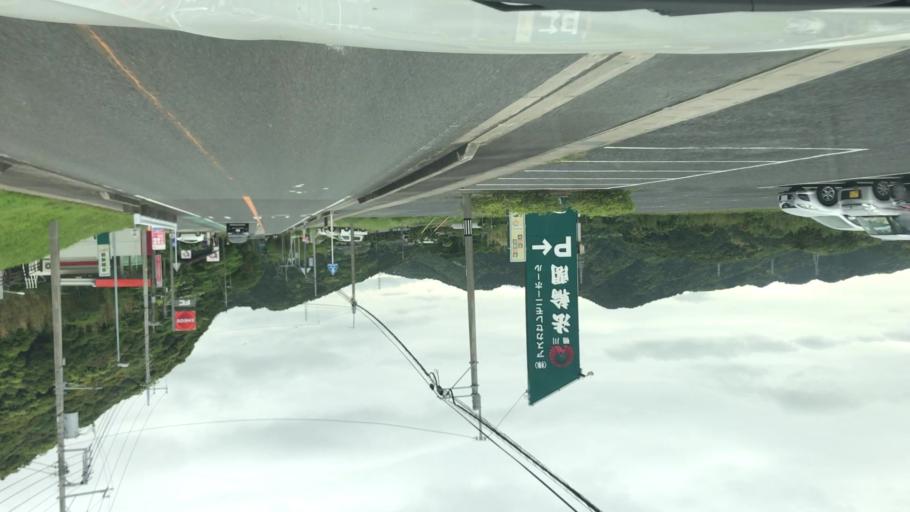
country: JP
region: Chiba
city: Kawaguchi
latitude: 35.1258
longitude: 140.0802
